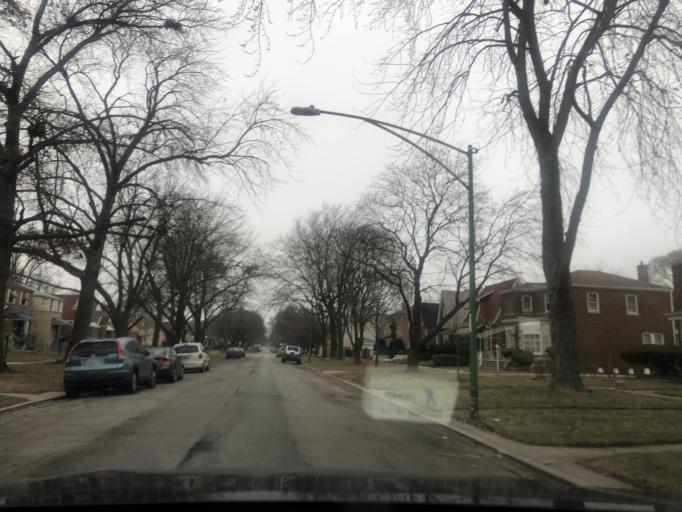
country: US
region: Illinois
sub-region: Cook County
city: Evergreen Park
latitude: 41.7422
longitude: -87.6212
